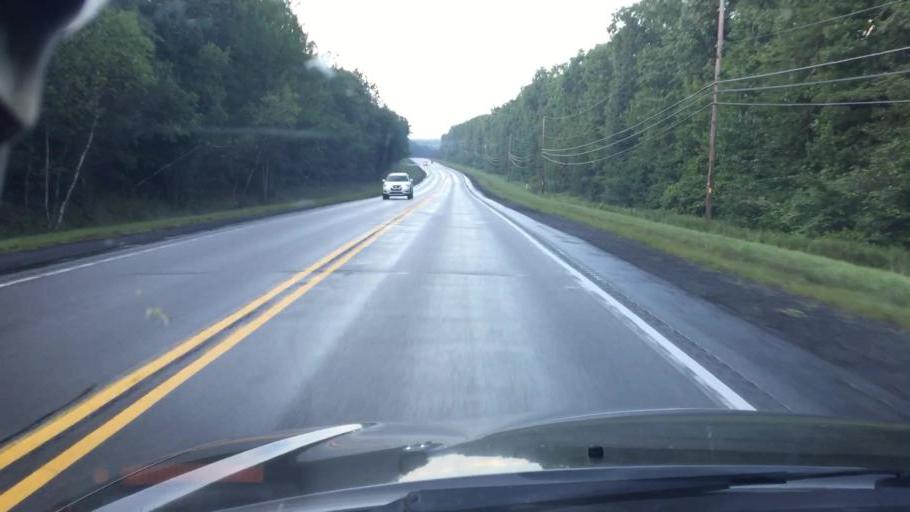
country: US
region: Pennsylvania
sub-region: Carbon County
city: Jim Thorpe
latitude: 40.9169
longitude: -75.6684
